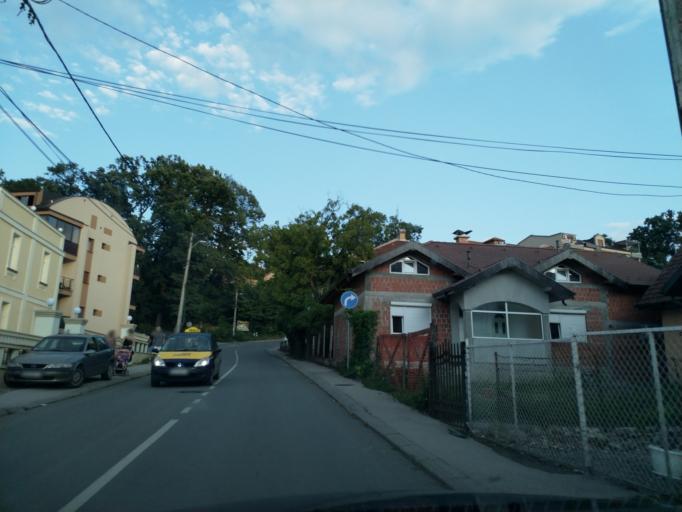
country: RS
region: Central Serbia
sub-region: Raski Okrug
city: Vrnjacka Banja
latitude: 43.6239
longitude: 20.8970
